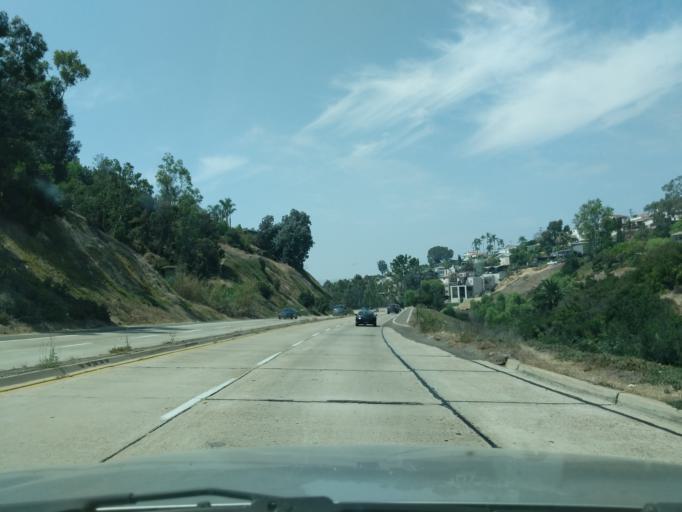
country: US
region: California
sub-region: San Diego County
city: San Diego
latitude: 32.7474
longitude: -117.1762
